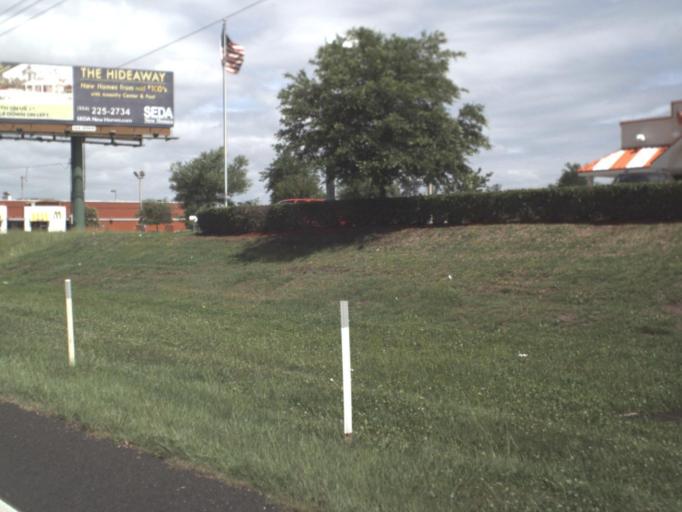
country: US
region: Florida
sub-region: Nassau County
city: Yulee
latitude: 30.6271
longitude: -81.5506
